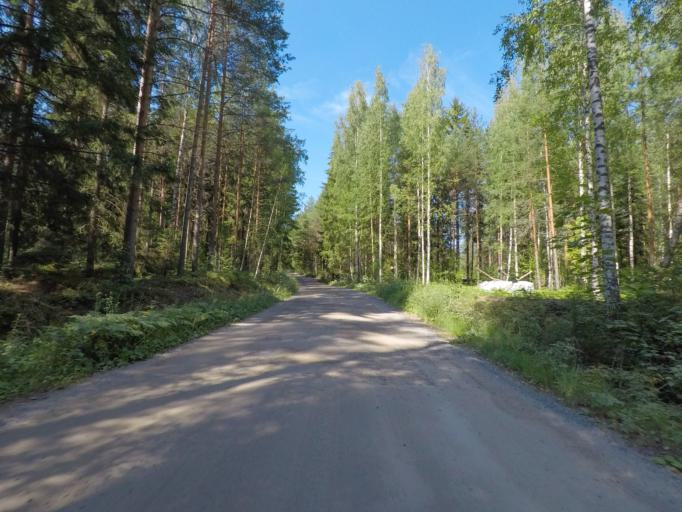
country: FI
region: Southern Savonia
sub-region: Mikkeli
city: Puumala
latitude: 61.4251
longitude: 28.0361
